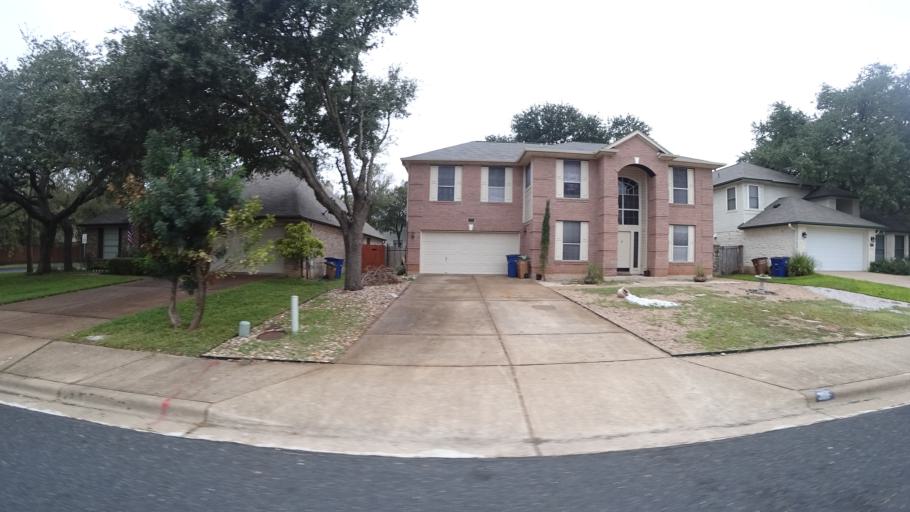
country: US
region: Texas
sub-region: Travis County
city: Shady Hollow
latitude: 30.1881
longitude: -97.8401
